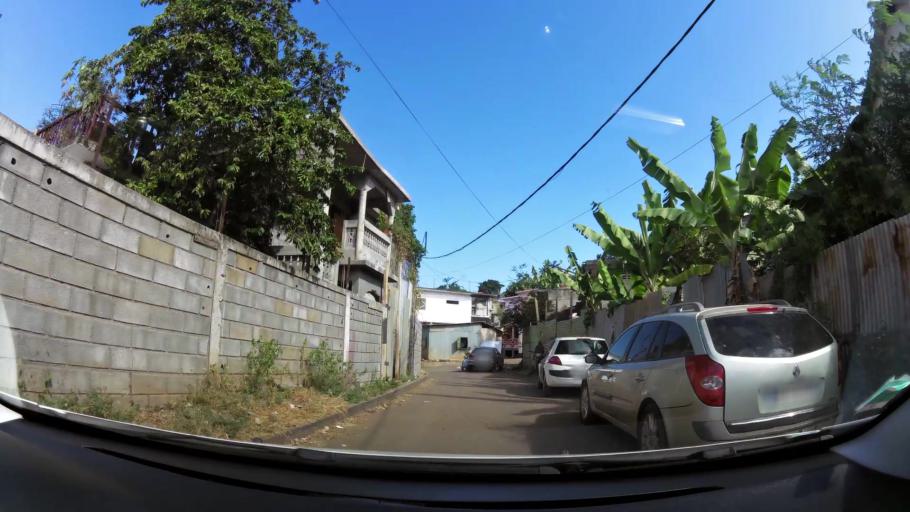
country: YT
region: Mamoudzou
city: Mamoudzou
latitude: -12.7841
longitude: 45.2190
